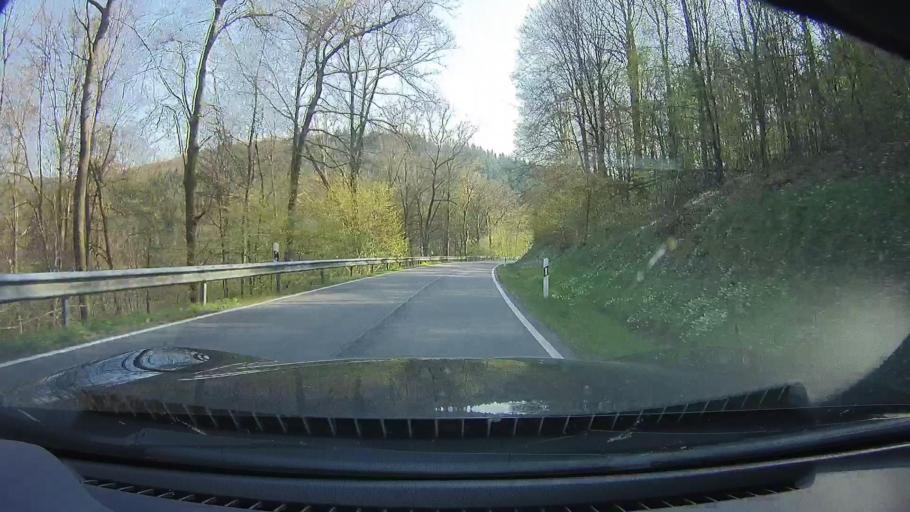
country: DE
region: Hesse
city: Hirschhorn
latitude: 49.4253
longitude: 8.9468
